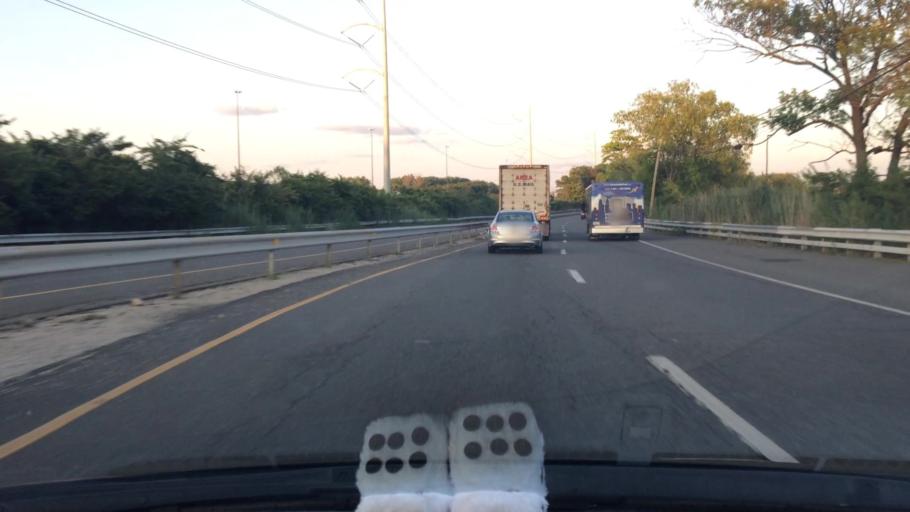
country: US
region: Pennsylvania
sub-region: Delaware County
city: Folcroft
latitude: 39.8753
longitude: -75.2714
